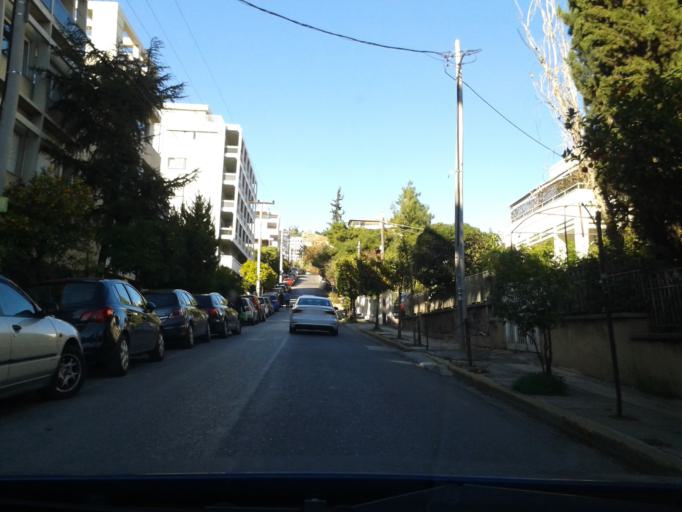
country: GR
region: Attica
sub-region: Nomarchia Athinas
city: Psychiko
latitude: 37.9991
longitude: 23.7681
